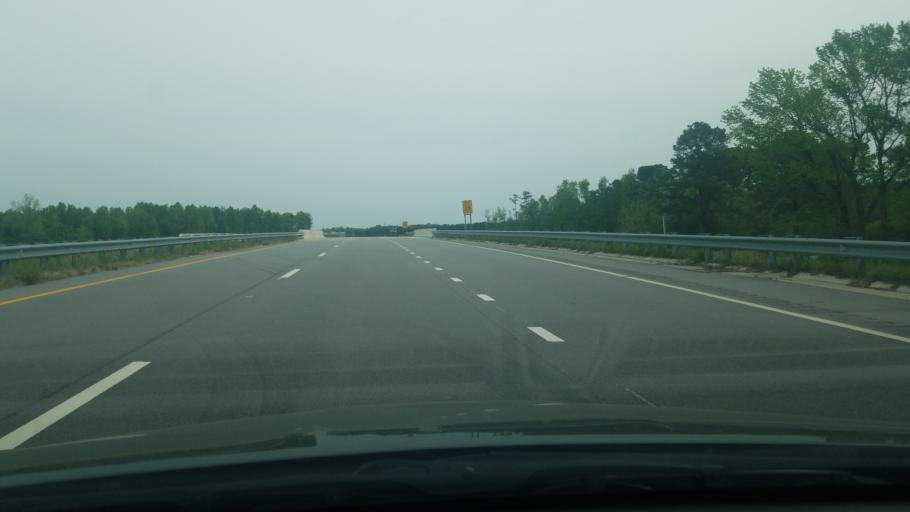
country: US
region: North Carolina
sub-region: Jones County
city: Maysville
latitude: 34.9985
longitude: -77.2331
